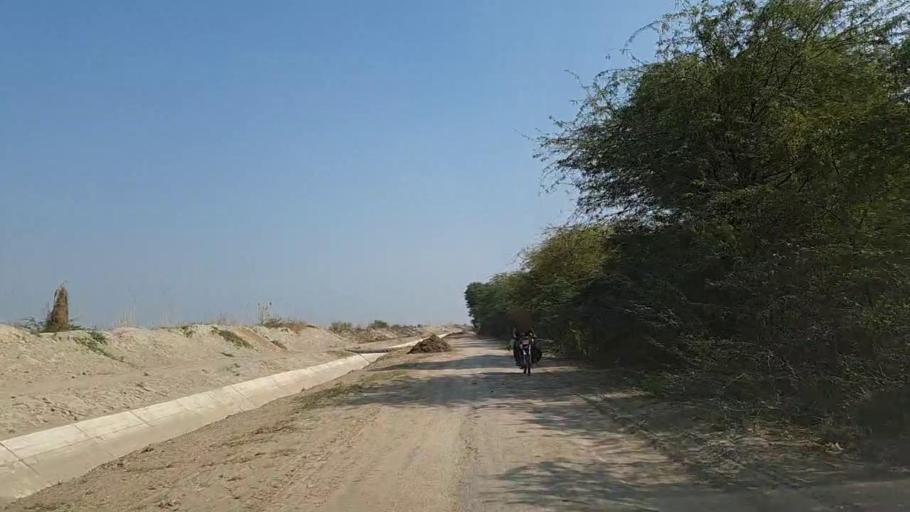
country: PK
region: Sindh
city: Jam Sahib
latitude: 26.2706
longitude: 68.5658
